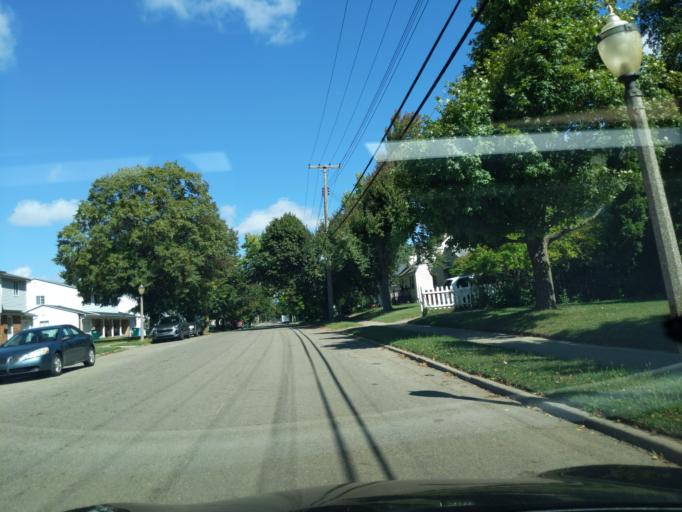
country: US
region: Michigan
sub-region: Ingham County
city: Lansing
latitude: 42.6953
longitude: -84.5527
